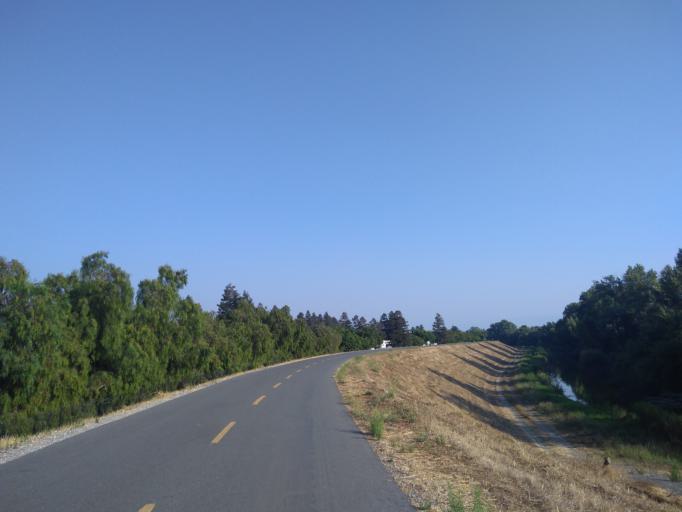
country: US
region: California
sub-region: Santa Clara County
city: Santa Clara
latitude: 37.3943
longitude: -121.9393
